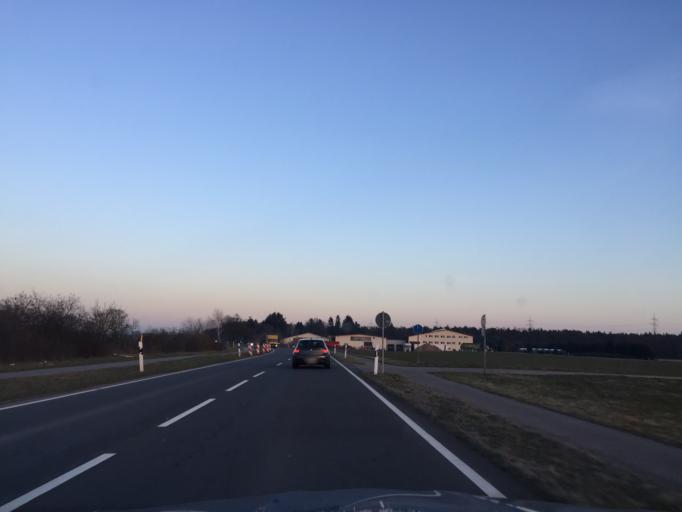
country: DE
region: Baden-Wuerttemberg
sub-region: Karlsruhe Region
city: Neulussheim
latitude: 49.2895
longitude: 8.5365
